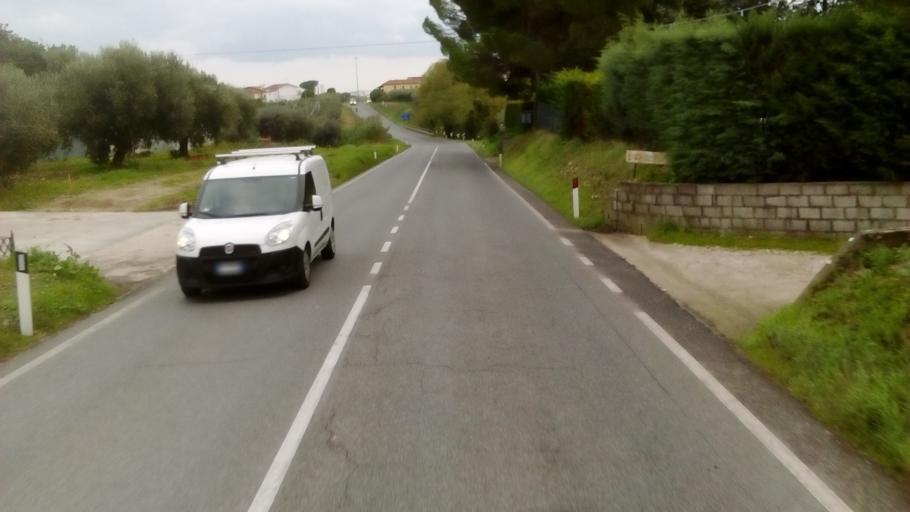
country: IT
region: Abruzzo
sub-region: Provincia di Chieti
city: Vasto
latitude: 42.1651
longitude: 14.6755
